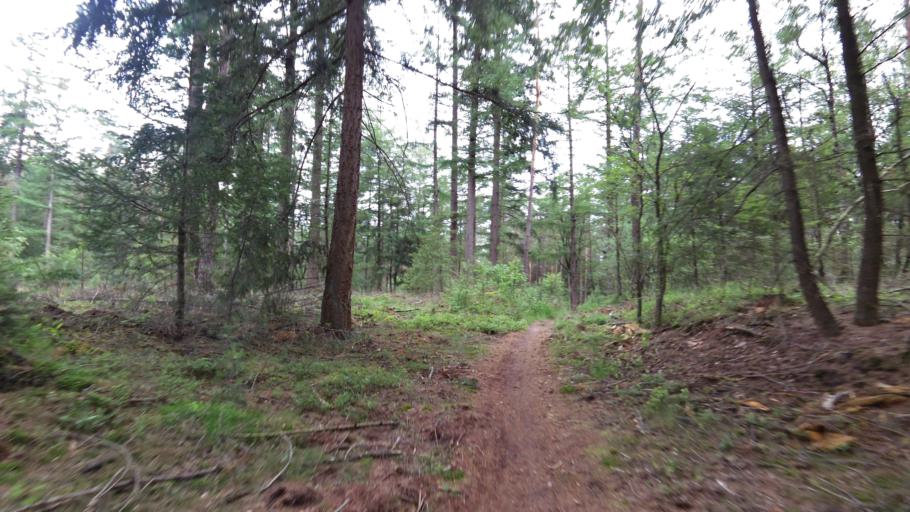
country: NL
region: Gelderland
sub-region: Gemeente Apeldoorn
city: Uddel
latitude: 52.2062
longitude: 5.8161
